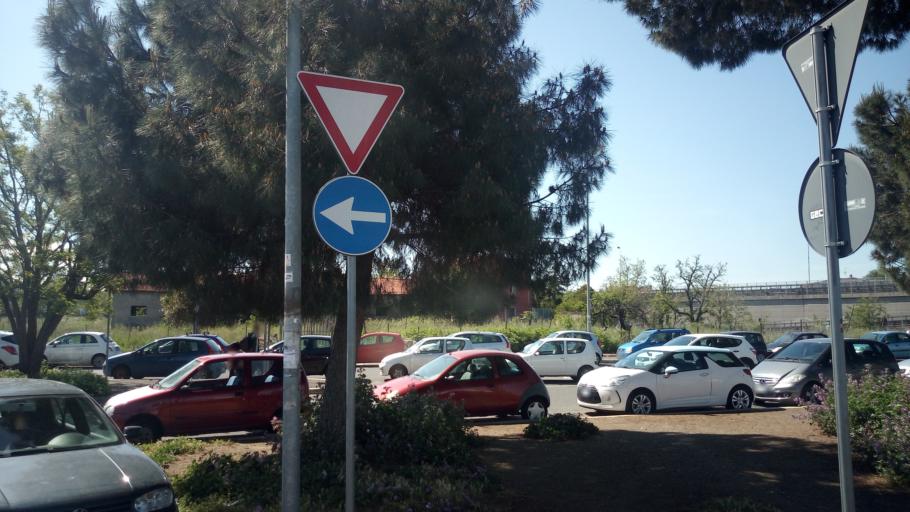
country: IT
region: Latium
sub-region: Citta metropolitana di Roma Capitale
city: Ciampino
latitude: 41.8420
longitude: 12.5872
